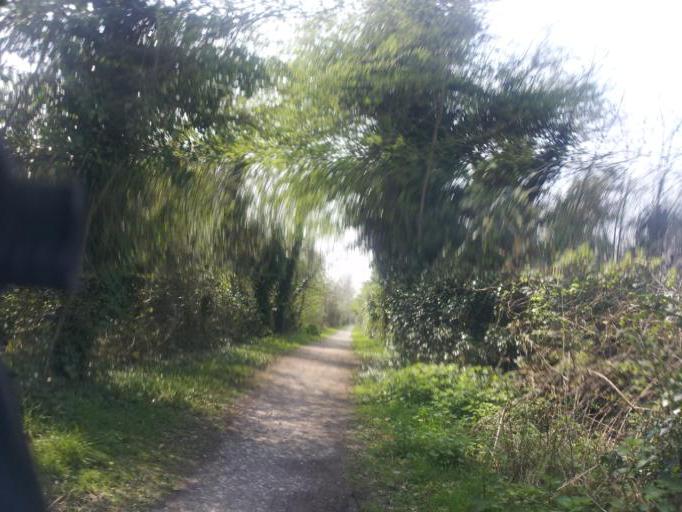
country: GB
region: England
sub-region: Kent
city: Cliffe
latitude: 51.4379
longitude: 0.4420
